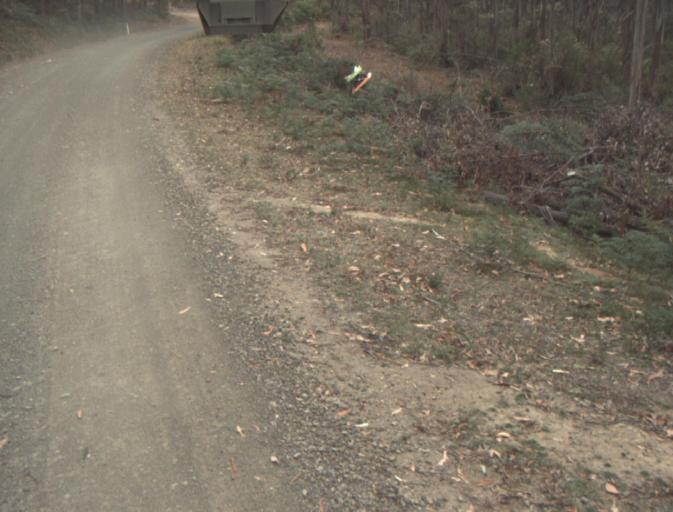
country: AU
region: Tasmania
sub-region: Dorset
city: Scottsdale
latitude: -41.4112
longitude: 147.5172
